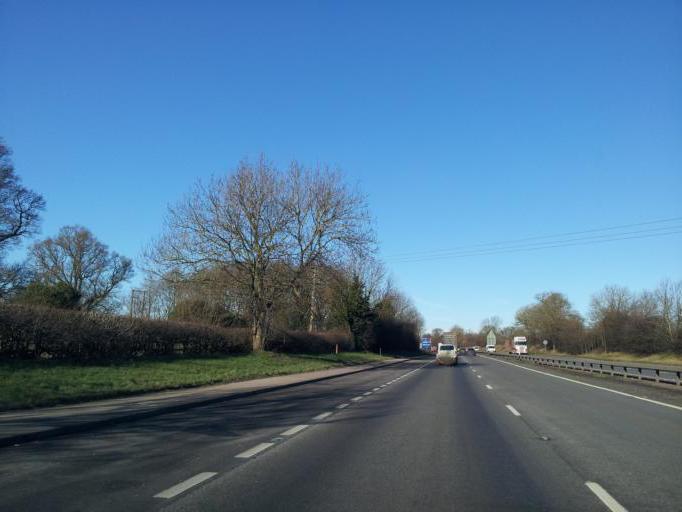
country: GB
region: England
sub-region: Derbyshire
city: Rodsley
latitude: 52.8867
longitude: -1.7595
